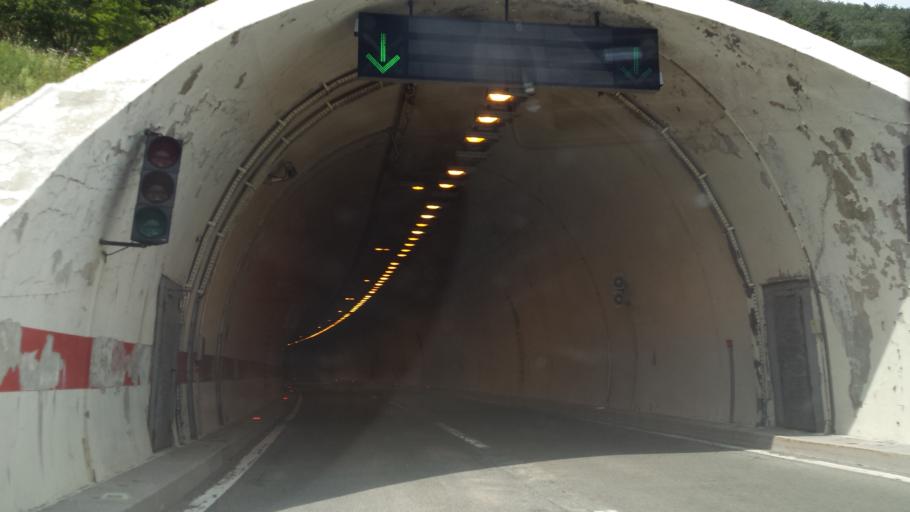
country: HR
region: Primorsko-Goranska
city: Hreljin
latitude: 45.3260
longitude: 14.6550
